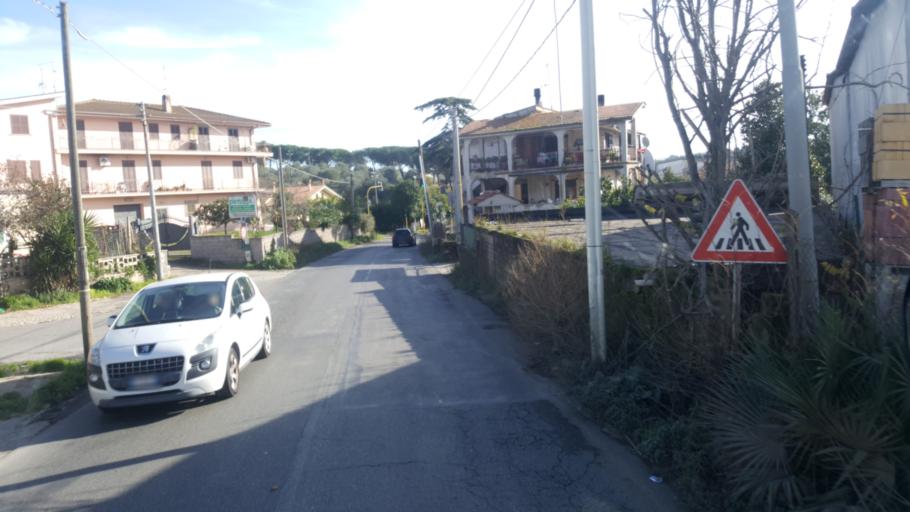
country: IT
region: Latium
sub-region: Citta metropolitana di Roma Capitale
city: Mantiglia di Ardea
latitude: 41.6796
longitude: 12.6228
